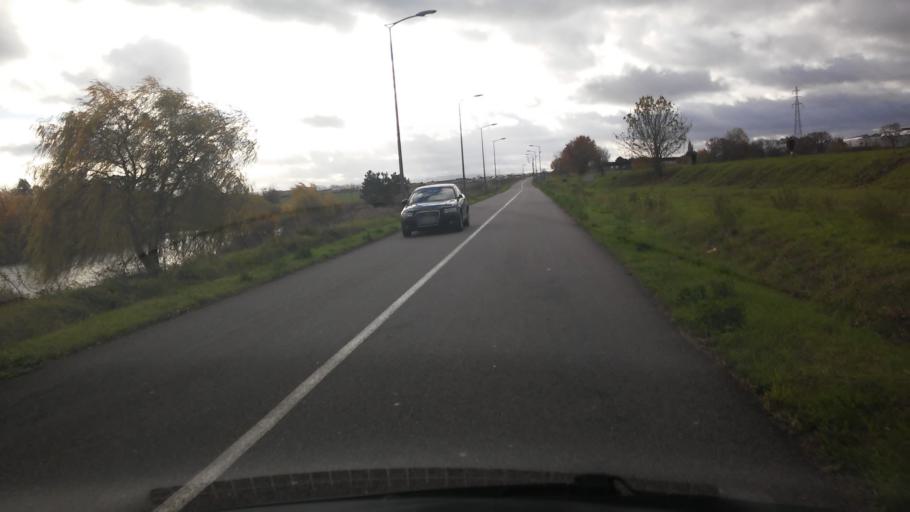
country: FR
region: Lorraine
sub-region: Departement de la Moselle
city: Talange
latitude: 49.2353
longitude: 6.1837
